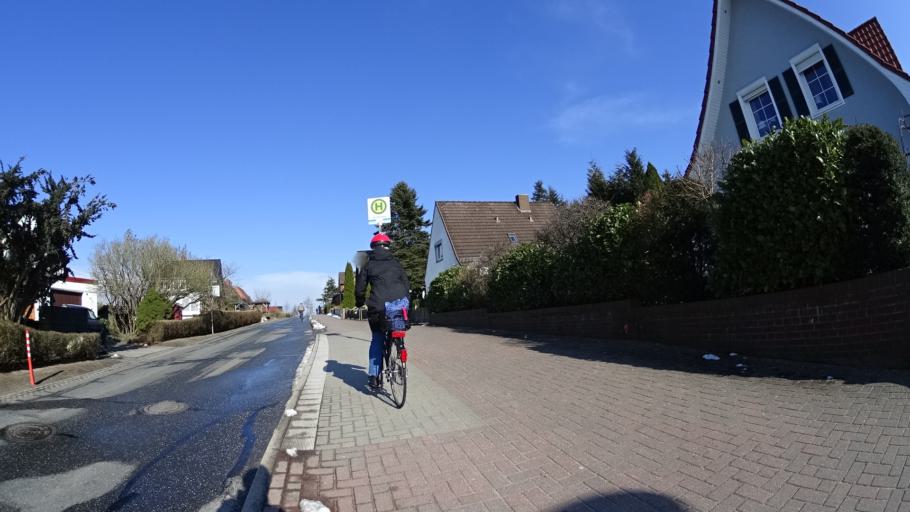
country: DE
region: Schleswig-Holstein
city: Schellhorn
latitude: 54.2407
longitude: 10.2918
